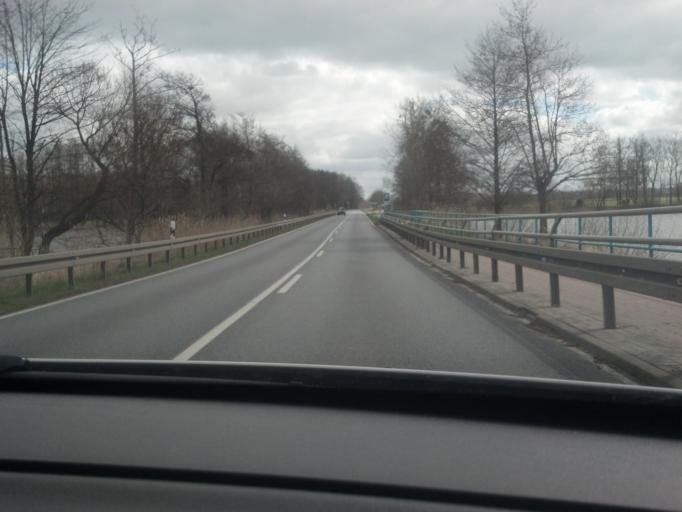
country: DE
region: Mecklenburg-Vorpommern
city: Rechlin
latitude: 53.3237
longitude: 12.6963
